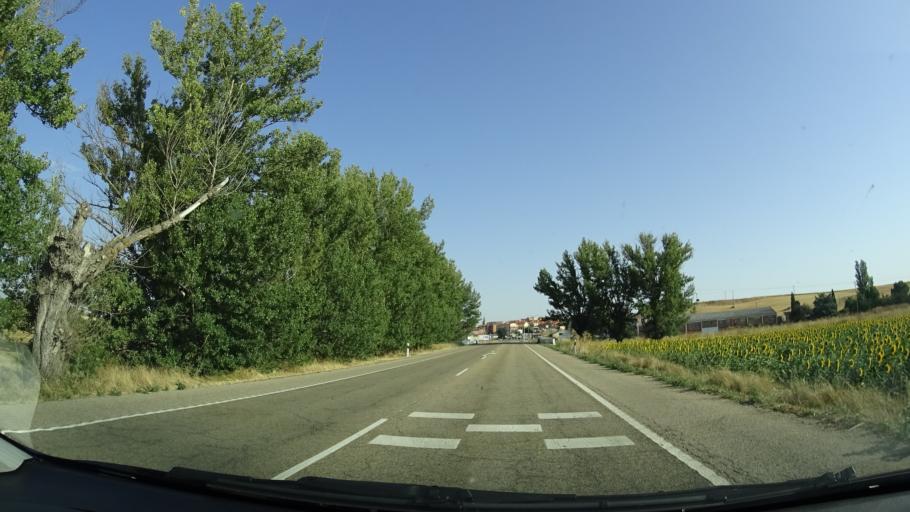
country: ES
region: Castille and Leon
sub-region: Provincia de Burgos
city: Lerma
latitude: 42.0168
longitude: -3.7531
